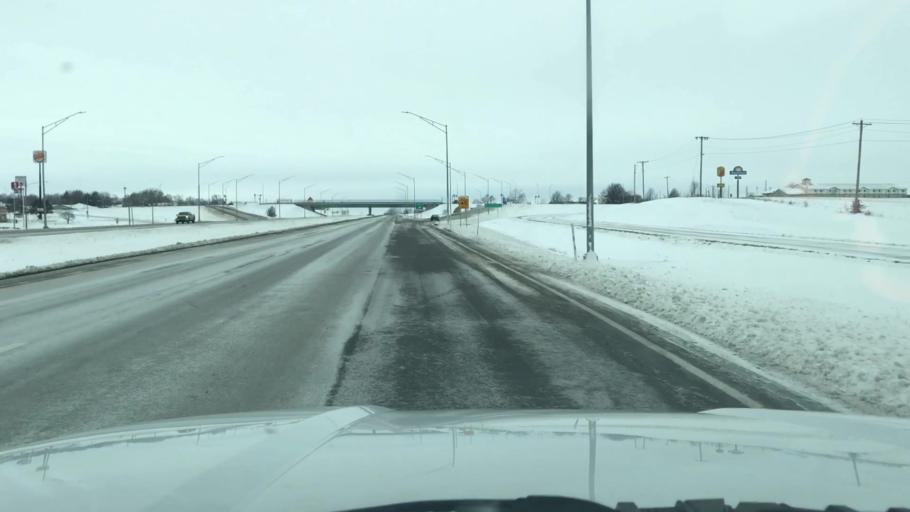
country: US
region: Missouri
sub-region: Clinton County
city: Cameron
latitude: 39.7543
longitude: -94.2281
